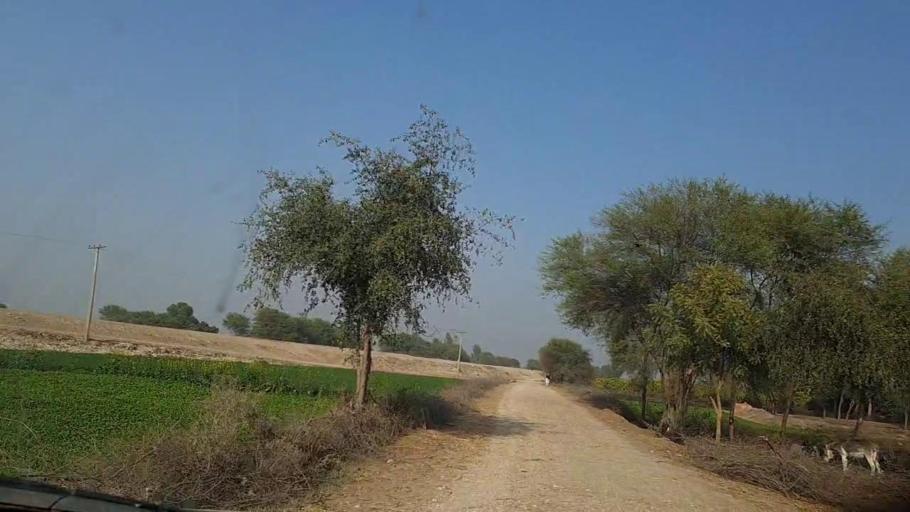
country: PK
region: Sindh
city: Moro
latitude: 26.8028
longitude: 67.9478
